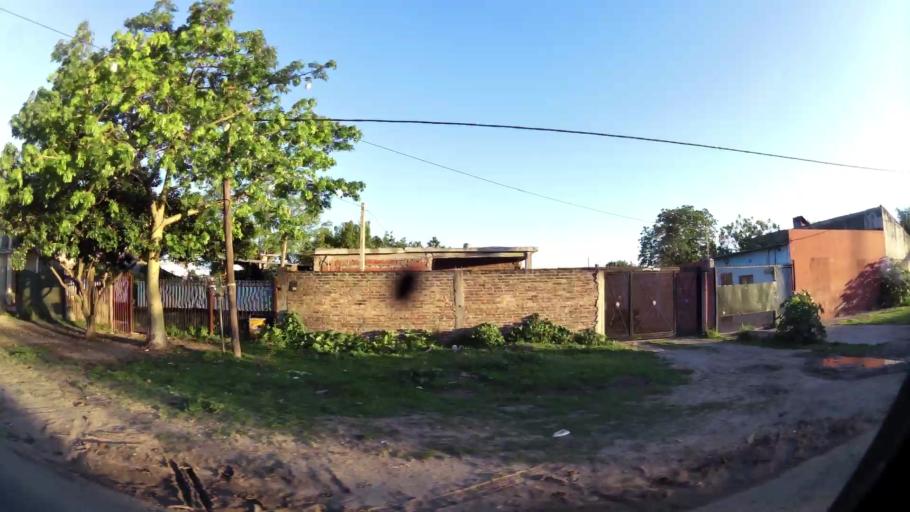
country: AR
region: Buenos Aires
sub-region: Partido de Almirante Brown
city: Adrogue
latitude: -34.7838
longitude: -58.3355
